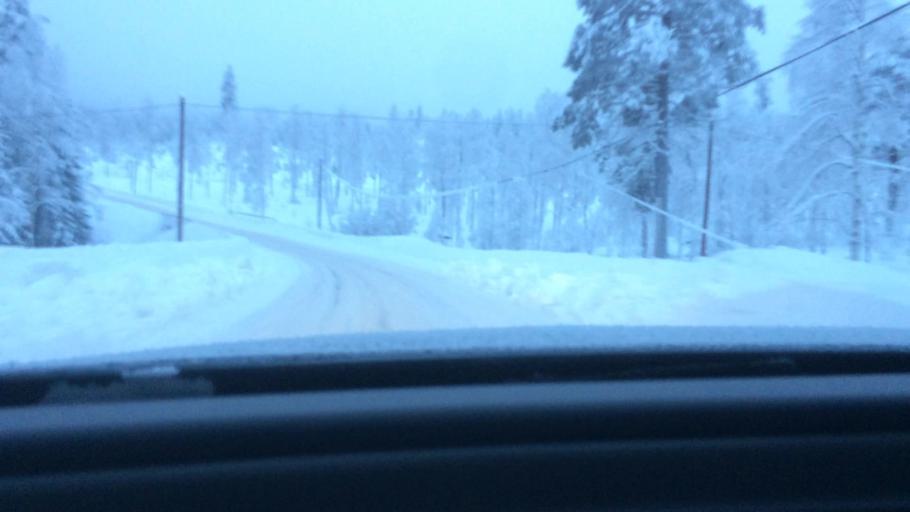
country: SE
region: Gaevleborg
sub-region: Ljusdals Kommun
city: Farila
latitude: 61.7643
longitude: 15.1499
